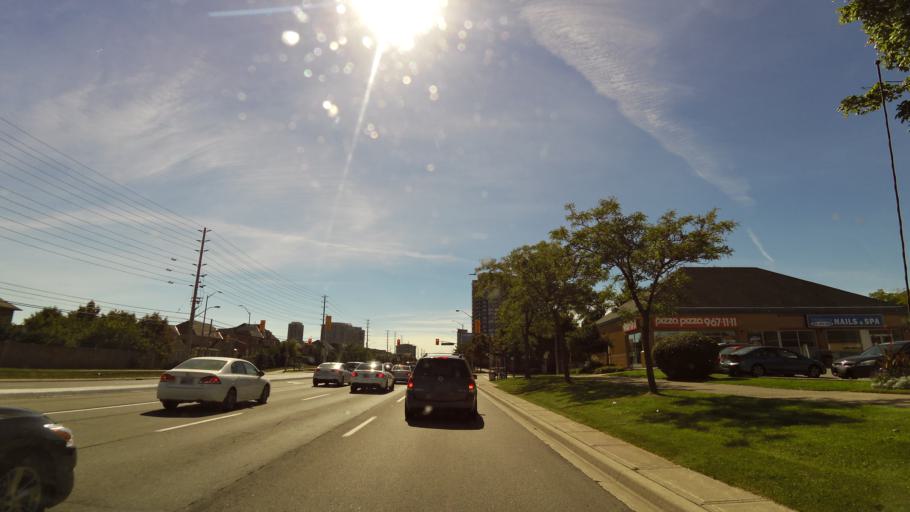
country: CA
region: Ontario
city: Mississauga
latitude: 43.6132
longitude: -79.6460
